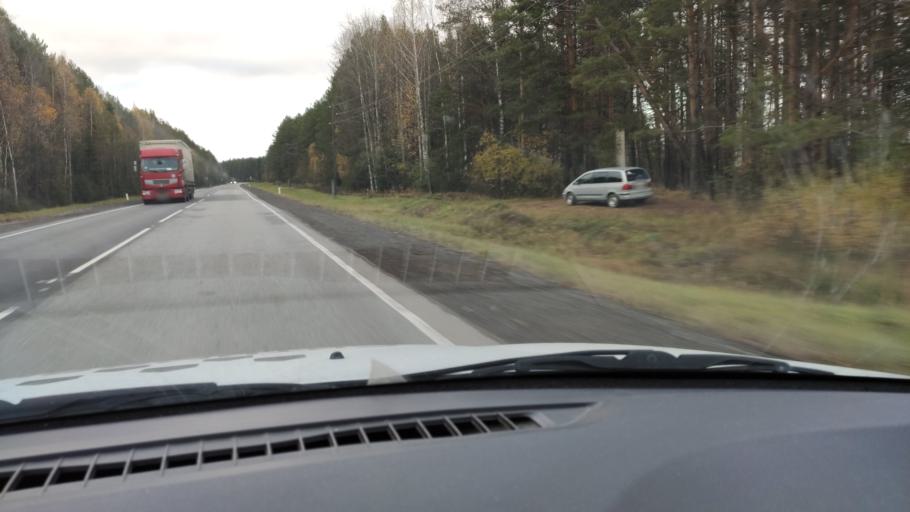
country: RU
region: Kirov
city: Belaya Kholunitsa
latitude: 58.8754
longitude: 50.8626
